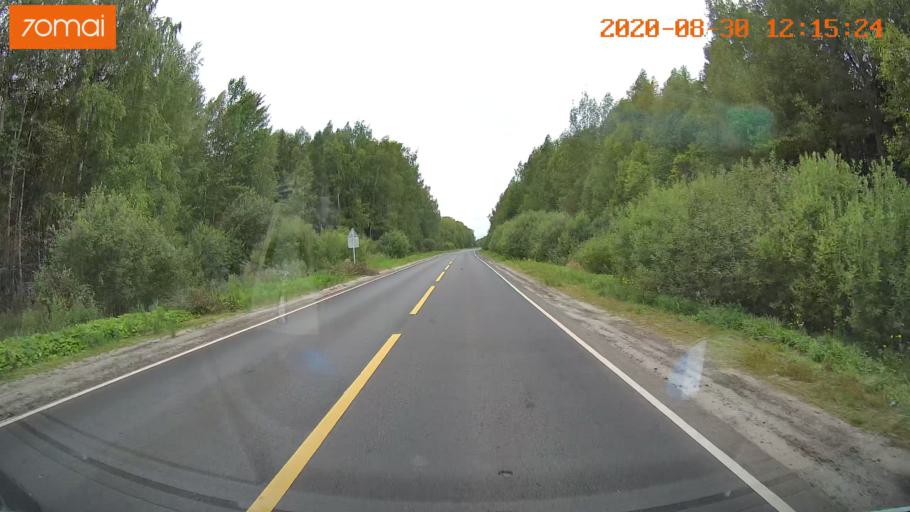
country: RU
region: Ivanovo
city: Yur'yevets
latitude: 57.3172
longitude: 43.0305
